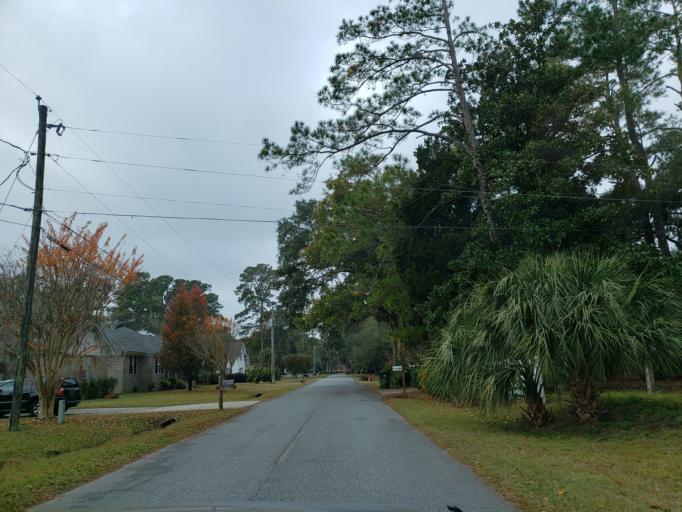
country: US
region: Georgia
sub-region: Chatham County
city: Wilmington Island
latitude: 32.0139
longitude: -80.9637
